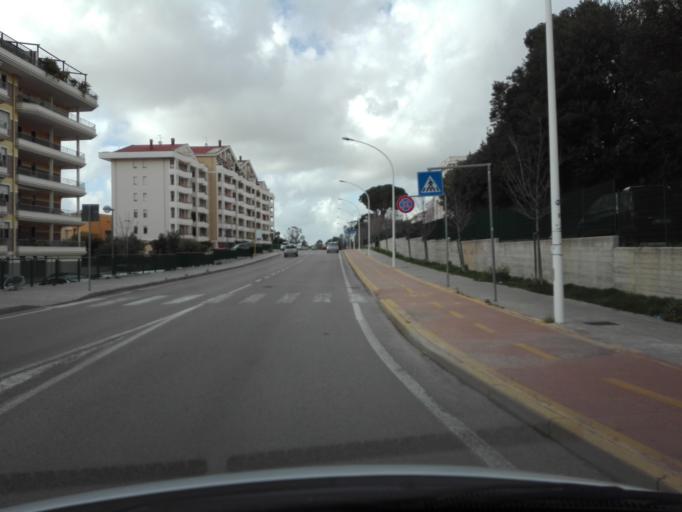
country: IT
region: Sardinia
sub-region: Provincia di Sassari
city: Sassari
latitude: 40.7141
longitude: 8.5840
